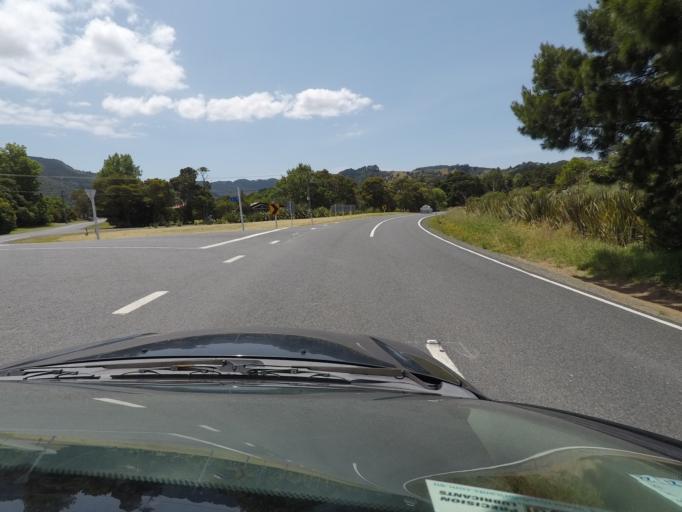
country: NZ
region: Auckland
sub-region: Auckland
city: Warkworth
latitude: -36.3224
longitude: 174.7309
